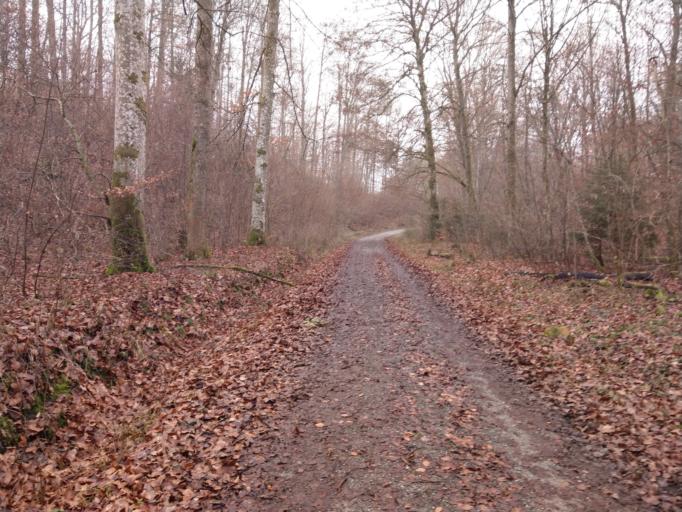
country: DE
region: Baden-Wuerttemberg
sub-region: Tuebingen Region
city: Dettenhausen
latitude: 48.6276
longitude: 9.1042
